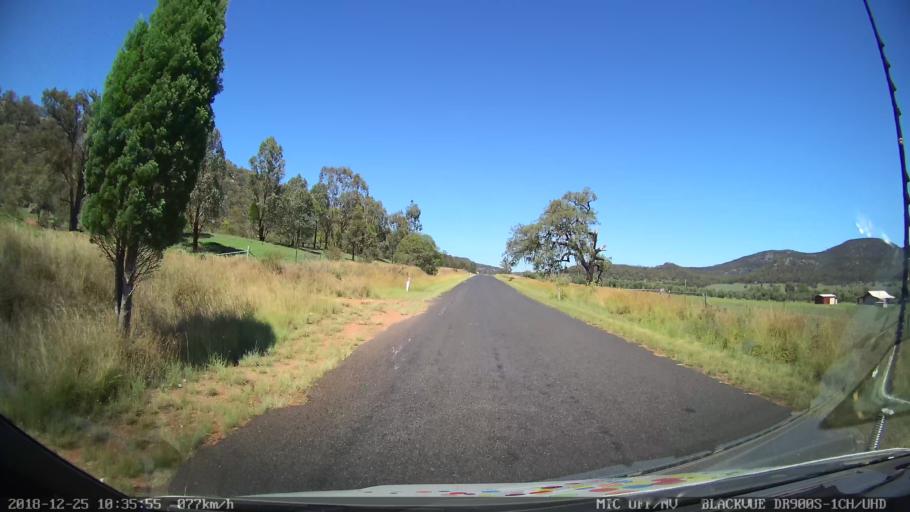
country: AU
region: New South Wales
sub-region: Upper Hunter Shire
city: Merriwa
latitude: -32.4018
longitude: 150.3915
